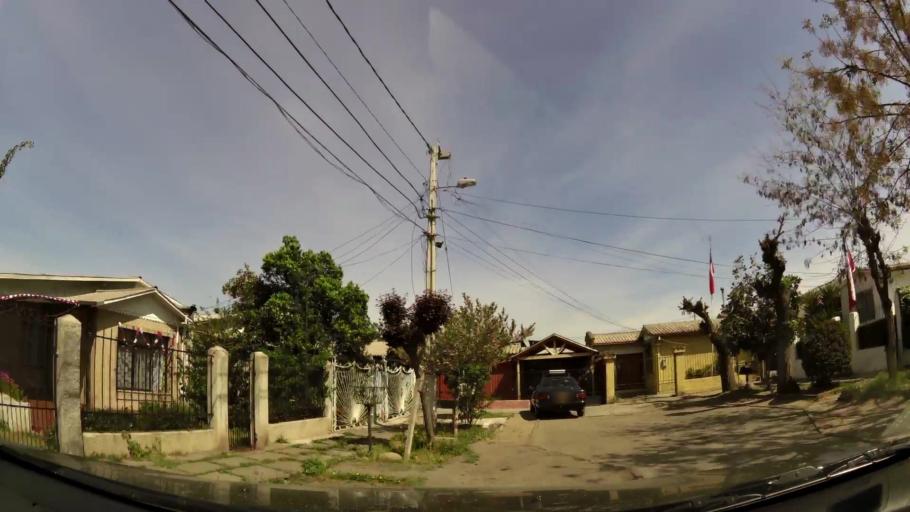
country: CL
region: Santiago Metropolitan
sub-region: Provincia de Cordillera
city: Puente Alto
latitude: -33.6186
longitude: -70.5806
